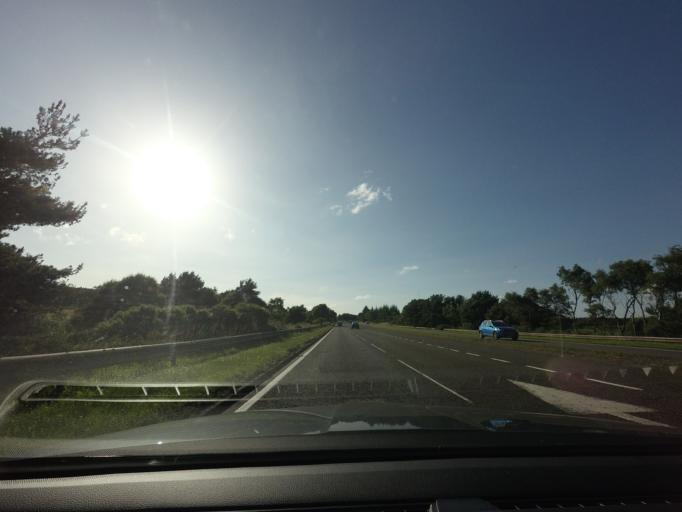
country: GB
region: Scotland
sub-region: Highland
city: Inverness
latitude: 57.5213
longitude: -4.3112
